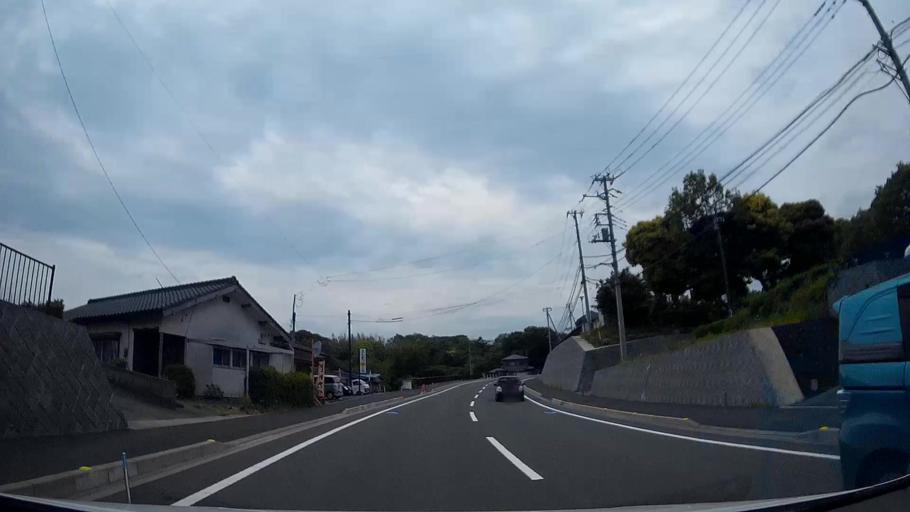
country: JP
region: Shizuoka
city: Ito
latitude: 34.8923
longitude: 139.1305
